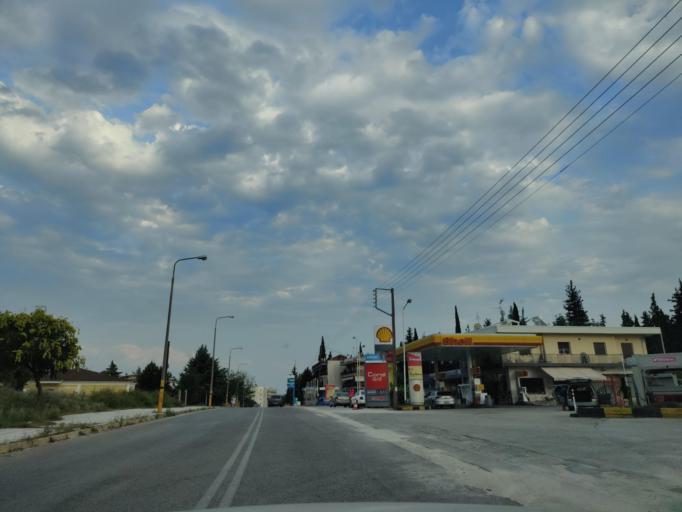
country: GR
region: East Macedonia and Thrace
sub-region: Nomos Dramas
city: Drama
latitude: 41.1514
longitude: 24.1337
